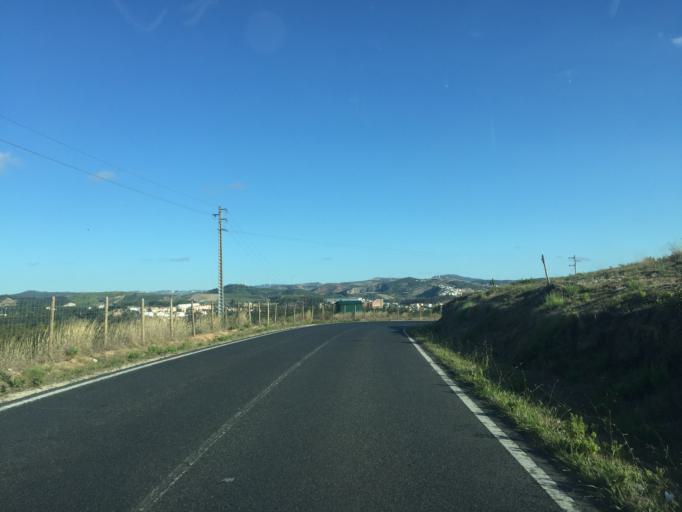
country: PT
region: Lisbon
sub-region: Torres Vedras
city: Torres Vedras
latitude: 39.1154
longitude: -9.2615
